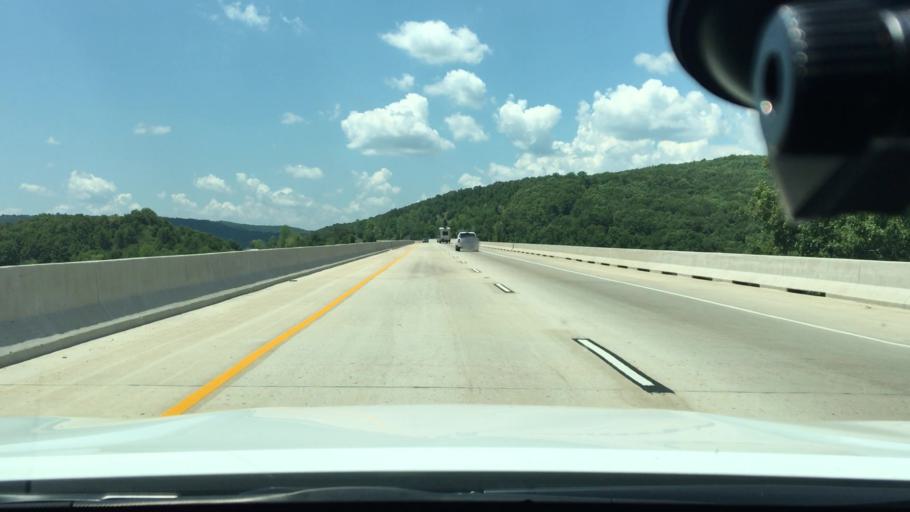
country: US
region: Arkansas
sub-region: Crawford County
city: Alma
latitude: 35.6932
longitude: -94.1824
